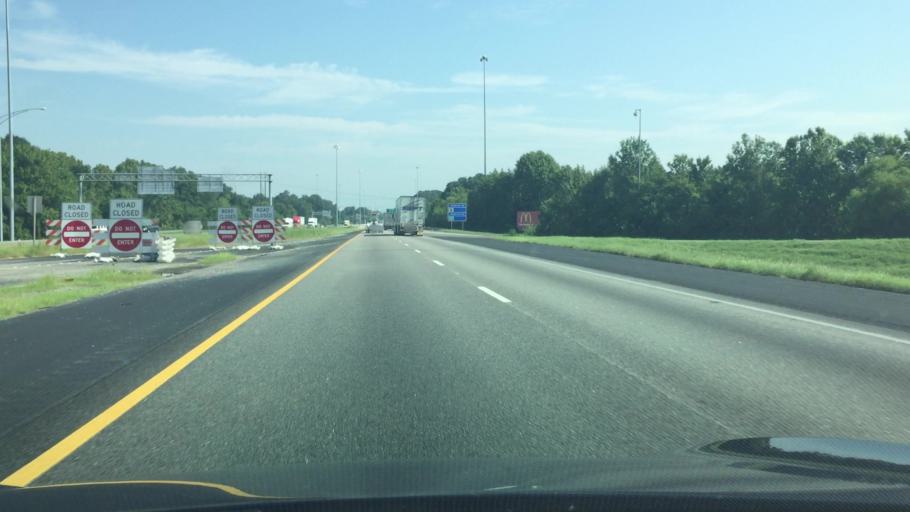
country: US
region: Alabama
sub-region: Montgomery County
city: Montgomery
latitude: 32.3127
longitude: -86.3369
